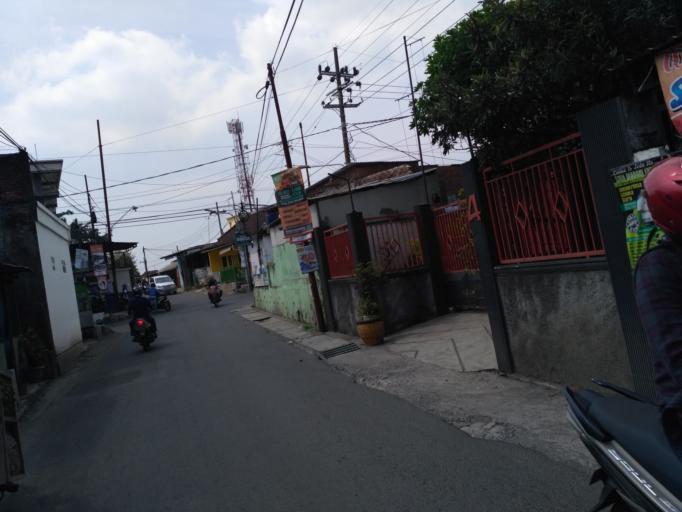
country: ID
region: East Java
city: Malang
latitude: -7.9361
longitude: 112.6274
